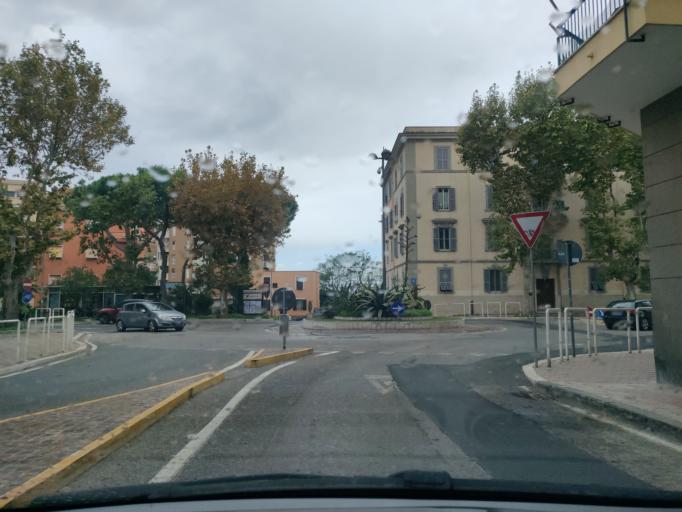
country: IT
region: Latium
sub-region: Citta metropolitana di Roma Capitale
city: Civitavecchia
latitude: 42.0888
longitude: 11.8046
